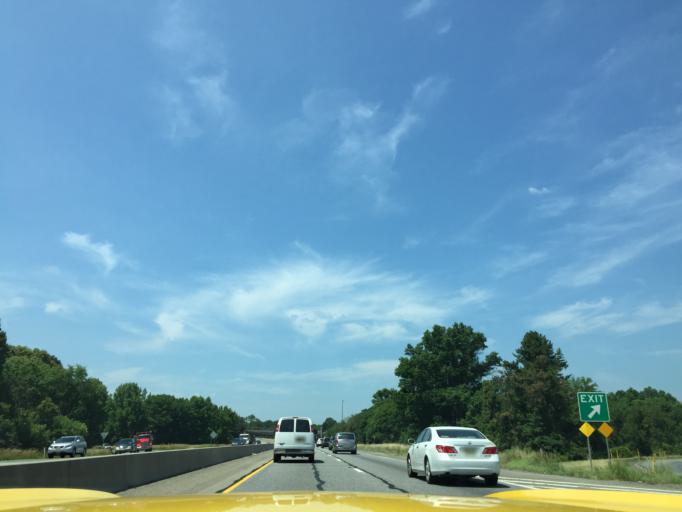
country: US
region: Pennsylvania
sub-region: Bucks County
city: Woodbourne
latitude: 40.1933
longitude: -74.8750
